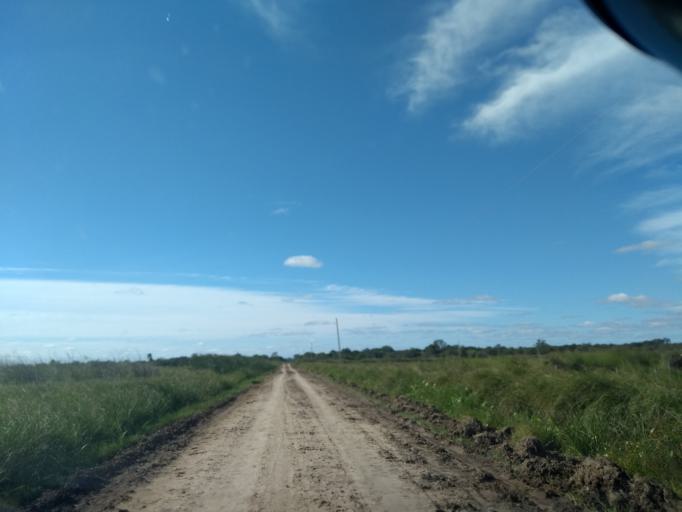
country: AR
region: Chaco
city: Colonia Benitez
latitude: -27.2897
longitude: -58.9343
